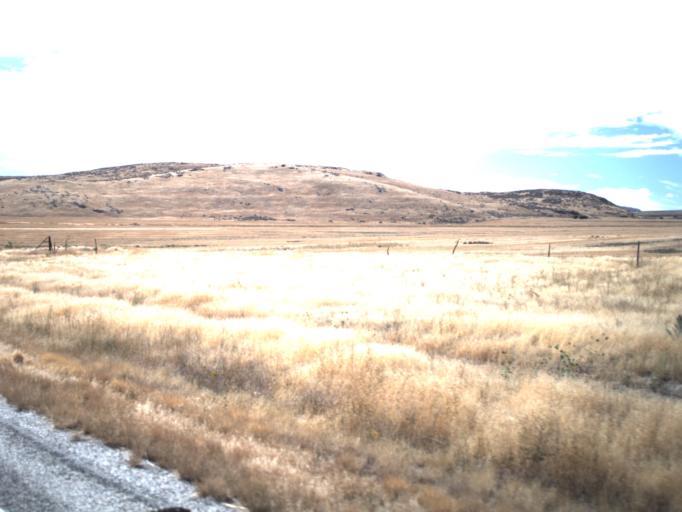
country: US
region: Utah
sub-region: Box Elder County
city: Tremonton
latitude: 41.7165
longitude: -112.4521
